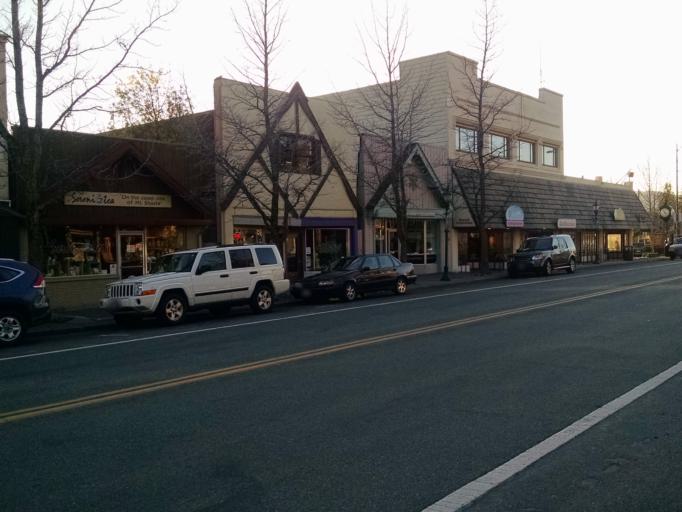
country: US
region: California
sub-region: Siskiyou County
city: Mount Shasta
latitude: 41.3137
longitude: -122.3129
